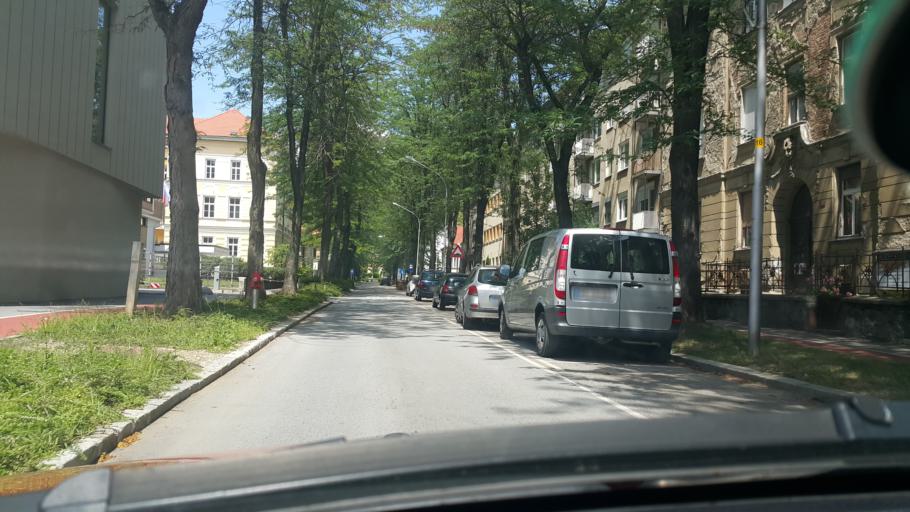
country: SI
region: Maribor
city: Maribor
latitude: 46.5634
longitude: 15.6516
